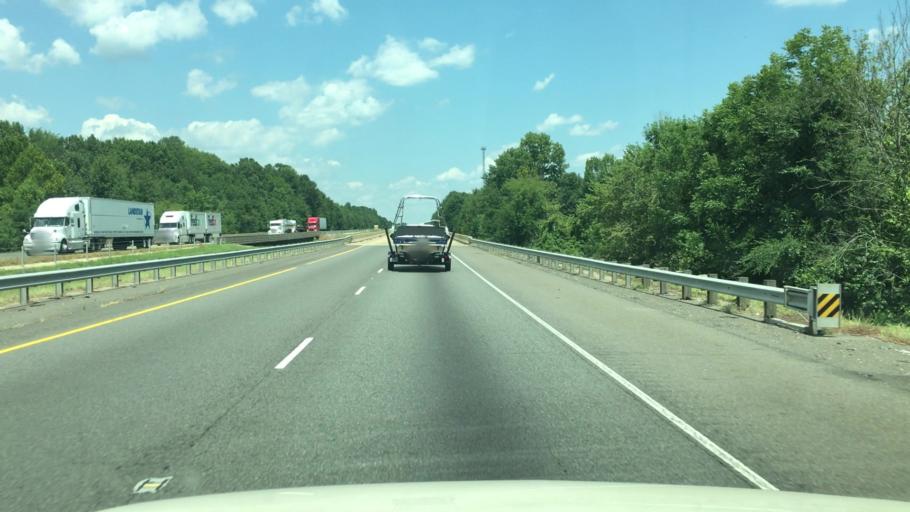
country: US
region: Arkansas
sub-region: Clark County
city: Gurdon
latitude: 34.0126
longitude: -93.1675
